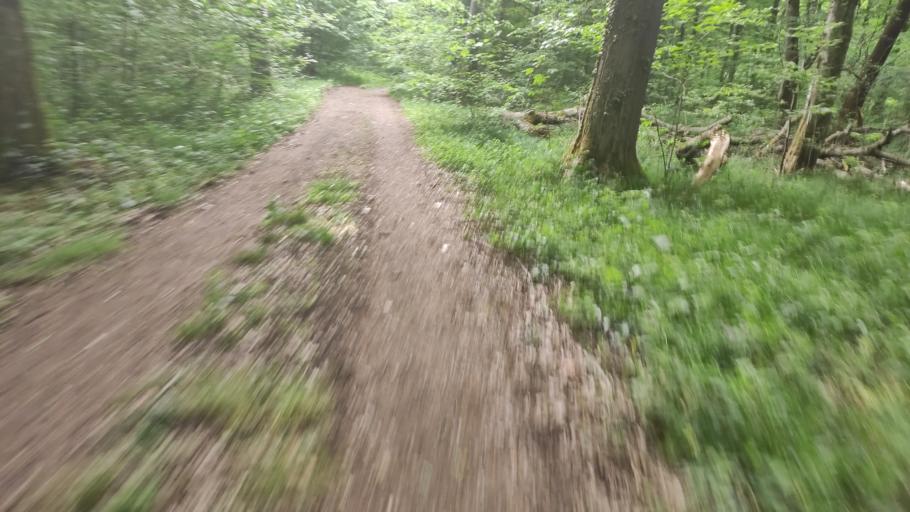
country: DE
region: Baden-Wuerttemberg
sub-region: Freiburg Region
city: Schallstadt
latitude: 47.9886
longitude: 7.7673
